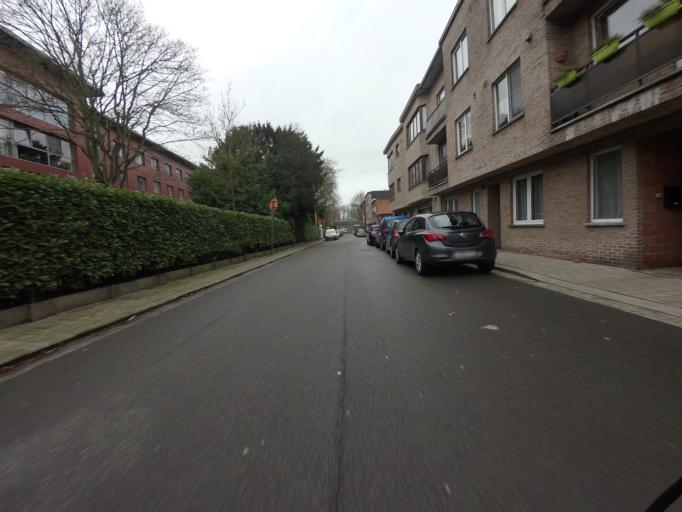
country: BE
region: Flanders
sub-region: Provincie Antwerpen
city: Hoboken
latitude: 51.1852
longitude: 4.3566
